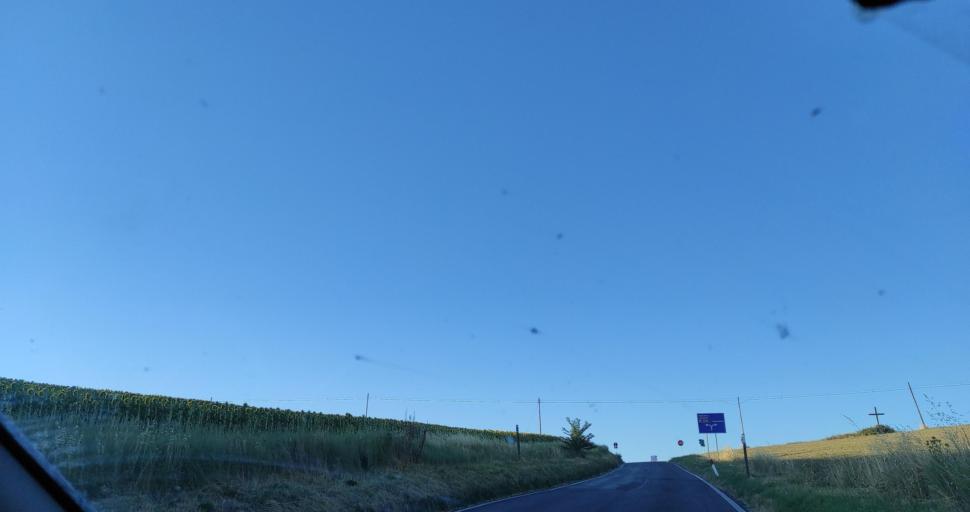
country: IT
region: The Marches
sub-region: Provincia di Macerata
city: Casette Verdini
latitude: 43.2302
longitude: 13.3958
